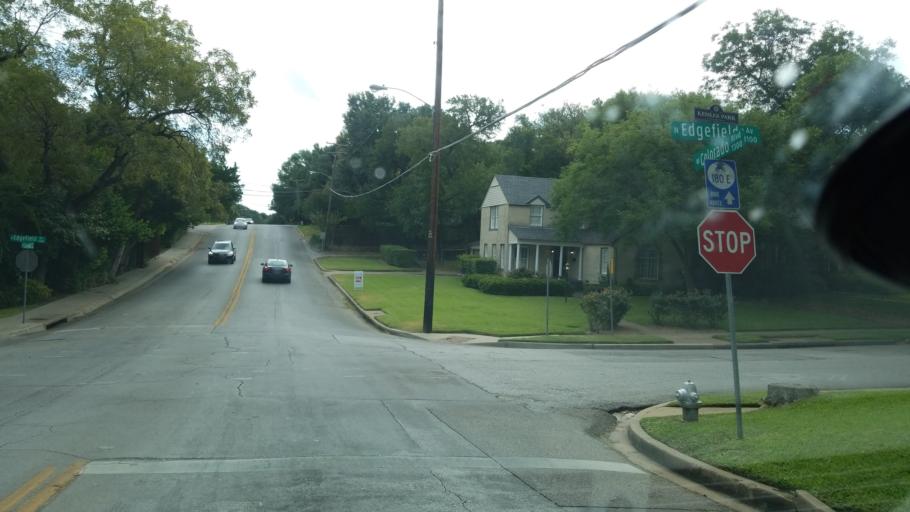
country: US
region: Texas
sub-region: Dallas County
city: Dallas
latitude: 32.7594
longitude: -96.8429
